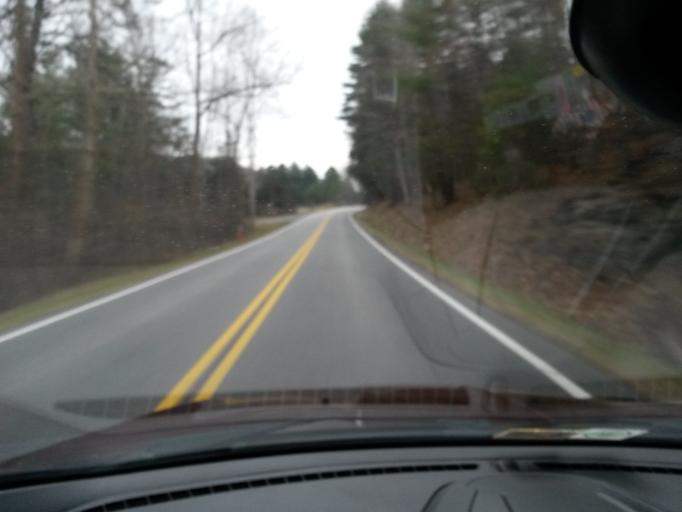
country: US
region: Virginia
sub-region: Bath County
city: Warm Springs
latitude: 38.0349
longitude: -79.6560
